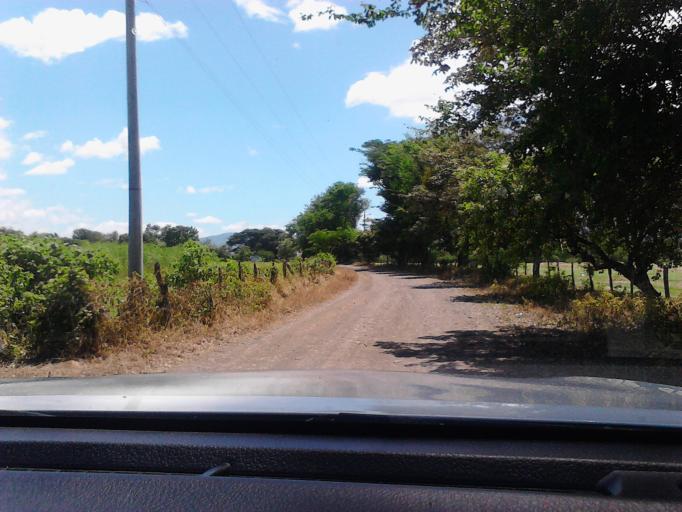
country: NI
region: Matagalpa
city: Ciudad Dario
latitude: 12.9003
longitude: -86.1422
